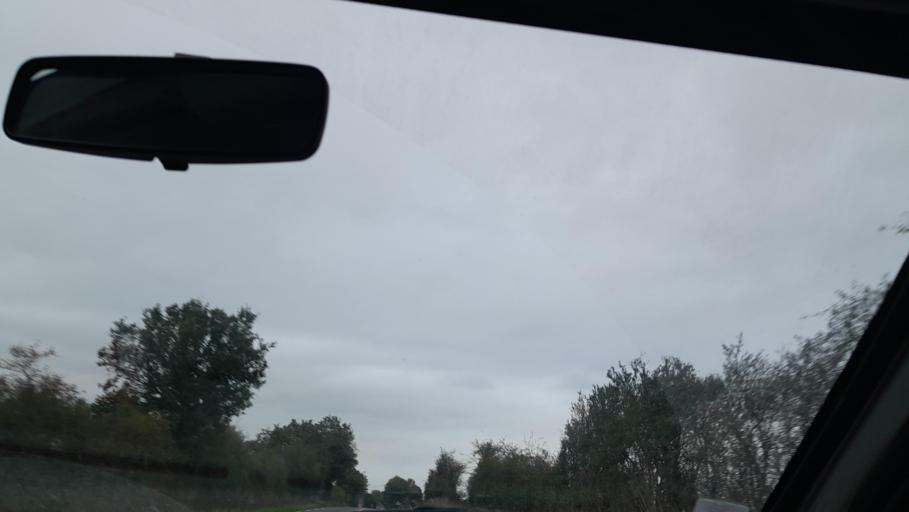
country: FR
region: Pays de la Loire
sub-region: Departement de Maine-et-Loire
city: Pouance
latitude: 47.6490
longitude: -1.2004
